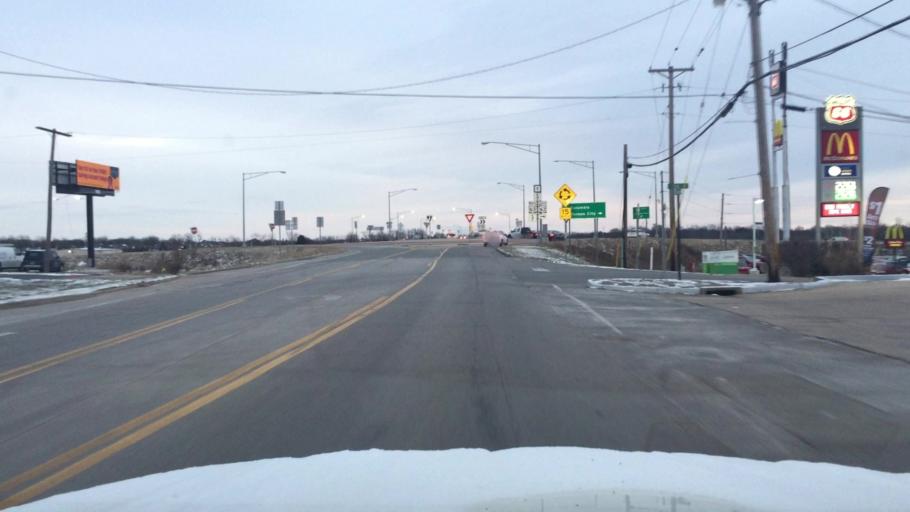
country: US
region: Missouri
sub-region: Boone County
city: Ashland
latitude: 38.7744
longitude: -92.2547
